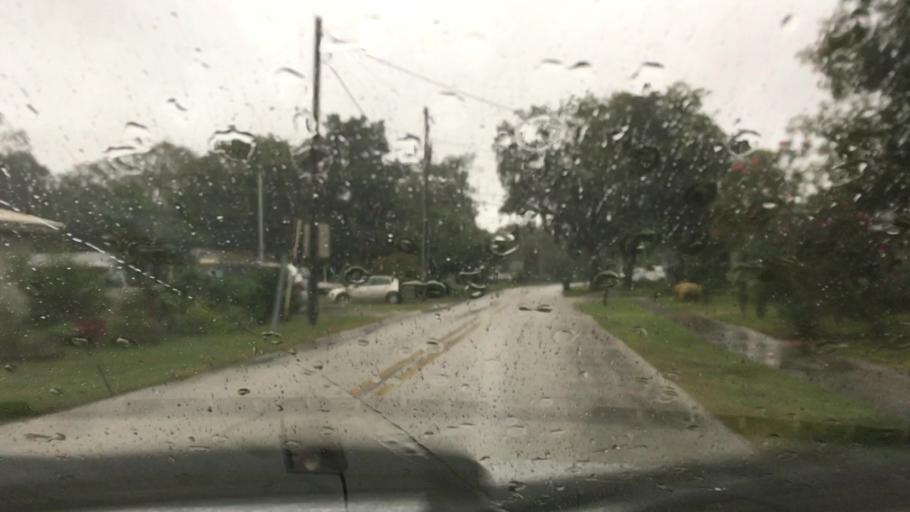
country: US
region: Florida
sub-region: Volusia County
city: Holly Hill
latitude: 29.2528
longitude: -81.0421
